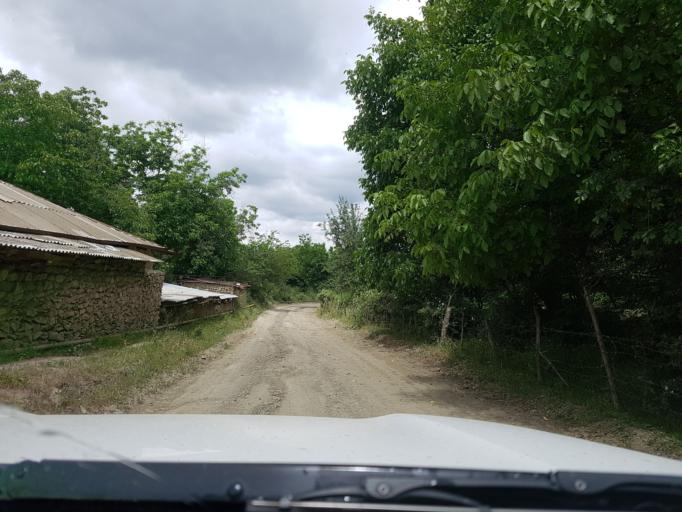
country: TM
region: Ahal
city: Baharly
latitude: 38.1947
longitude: 57.0059
